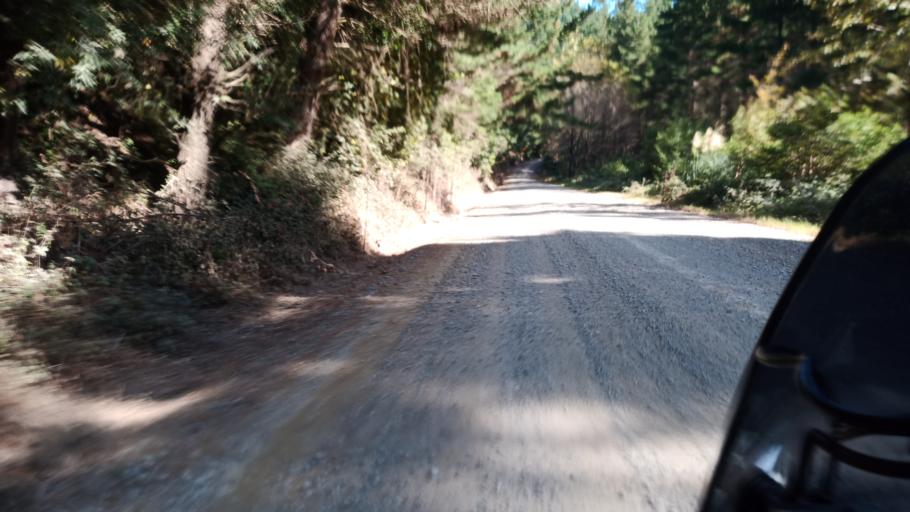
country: NZ
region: Hawke's Bay
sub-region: Wairoa District
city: Wairoa
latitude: -38.9295
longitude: 177.2227
